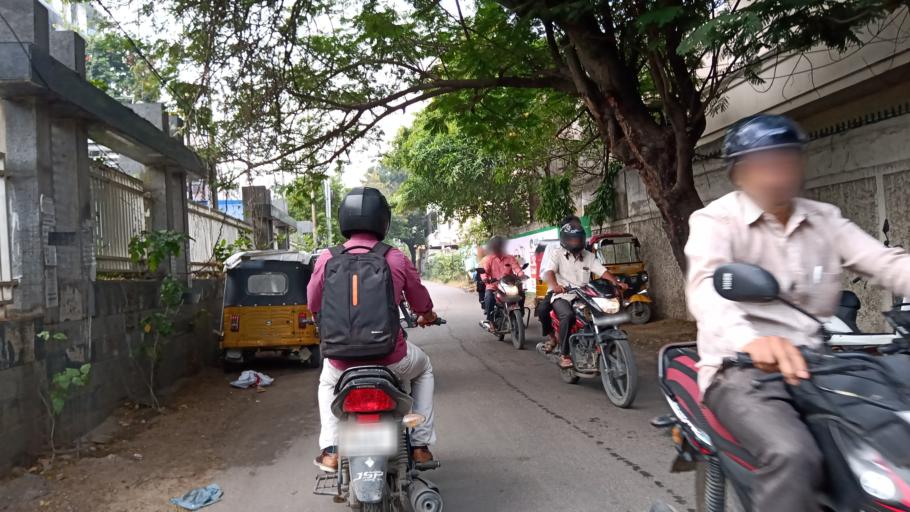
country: IN
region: Telangana
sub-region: Rangareddi
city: Kukatpalli
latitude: 17.4480
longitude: 78.4402
